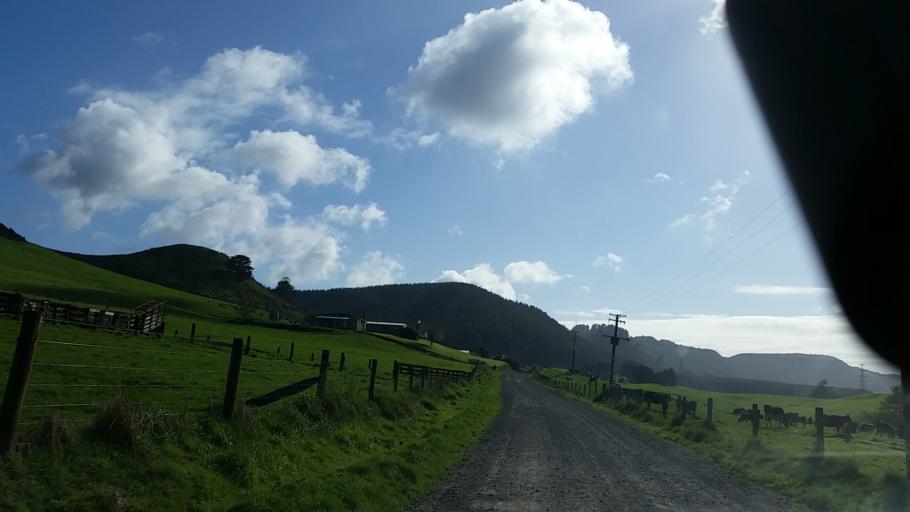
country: NZ
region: Bay of Plenty
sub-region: Rotorua District
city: Rotorua
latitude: -38.2319
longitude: 176.1581
